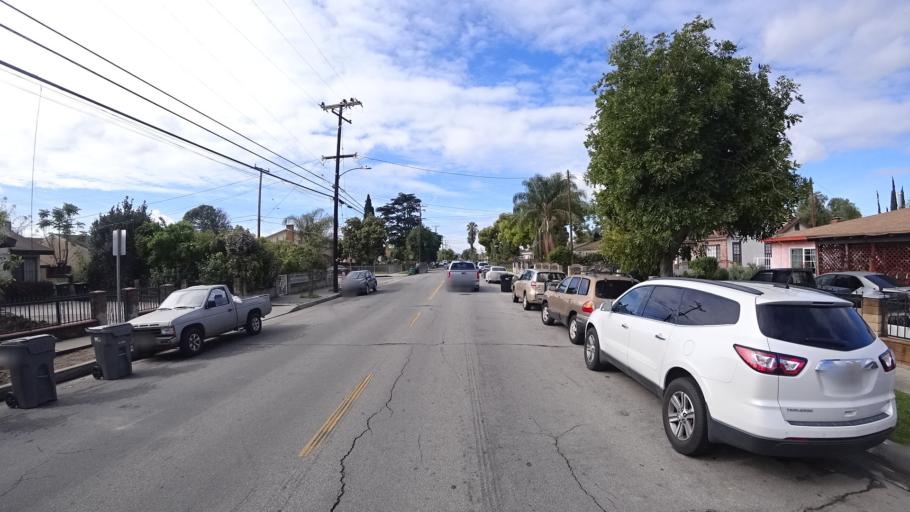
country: US
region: California
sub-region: Los Angeles County
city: Baldwin Park
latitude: 34.0760
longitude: -117.9709
